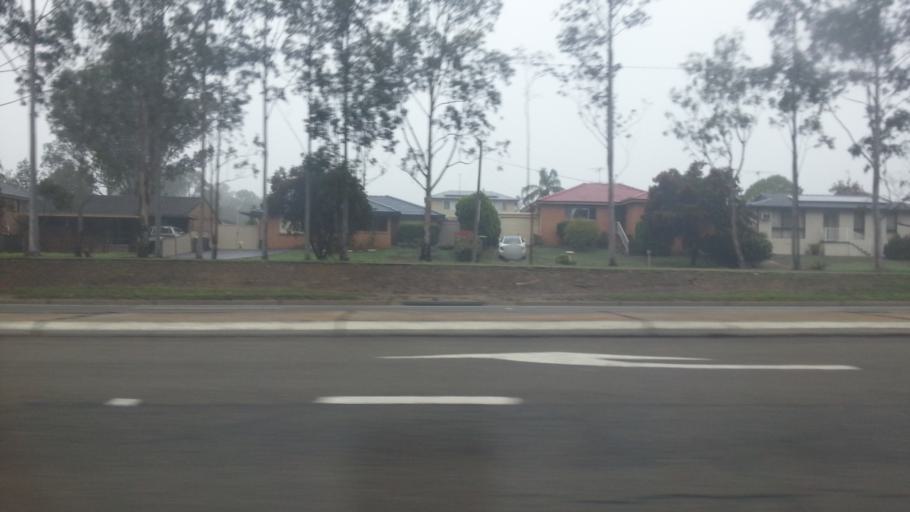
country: AU
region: New South Wales
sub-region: Penrith Municipality
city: Cambridge Park
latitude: -33.7375
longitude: 150.7170
